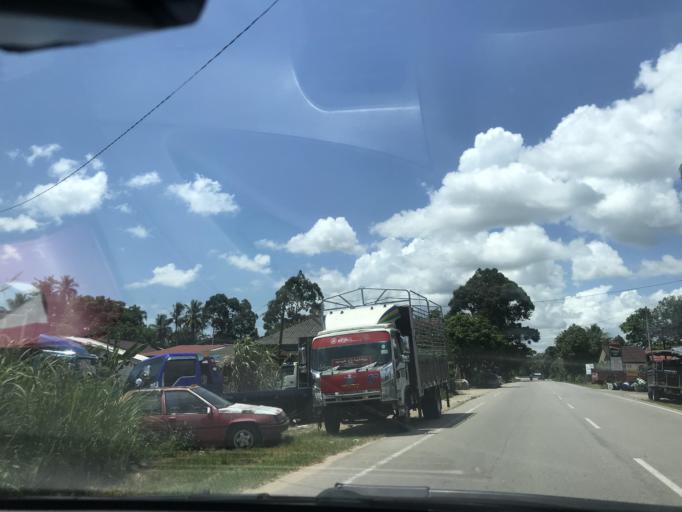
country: MY
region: Kelantan
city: Tumpat
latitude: 6.1985
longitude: 102.1301
